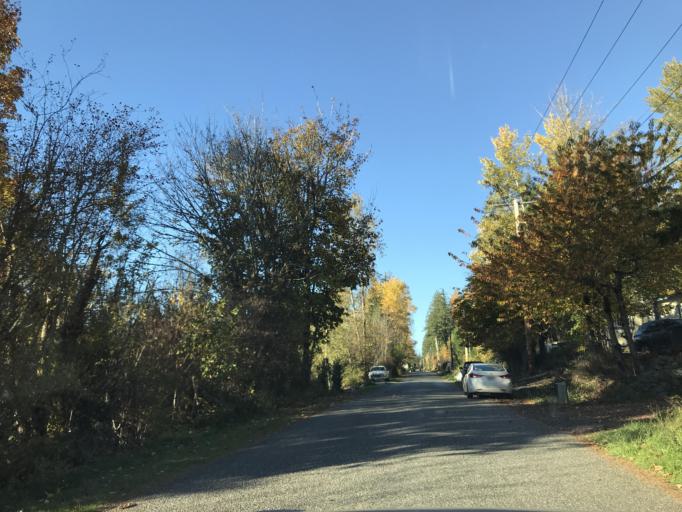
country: US
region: Washington
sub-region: Whatcom County
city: Geneva
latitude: 48.7684
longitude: -122.3990
